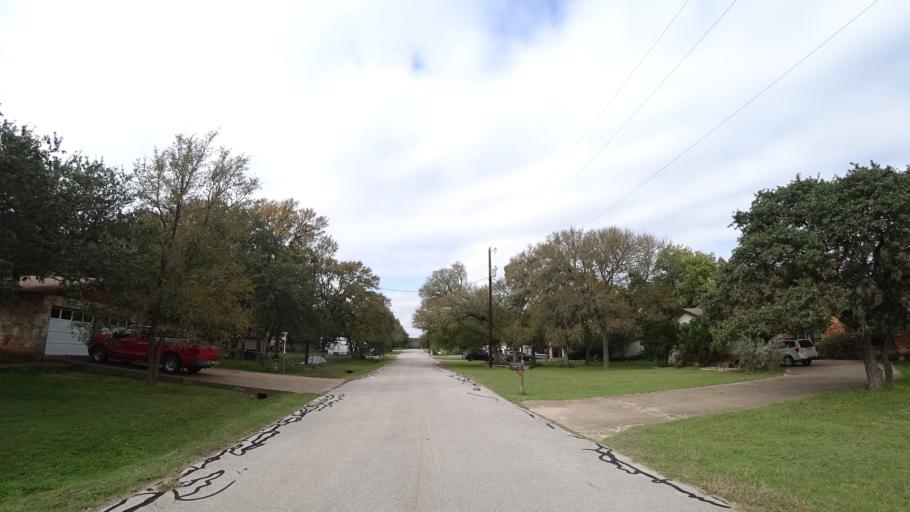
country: US
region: Texas
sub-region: Travis County
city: Shady Hollow
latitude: 30.1390
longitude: -97.8874
